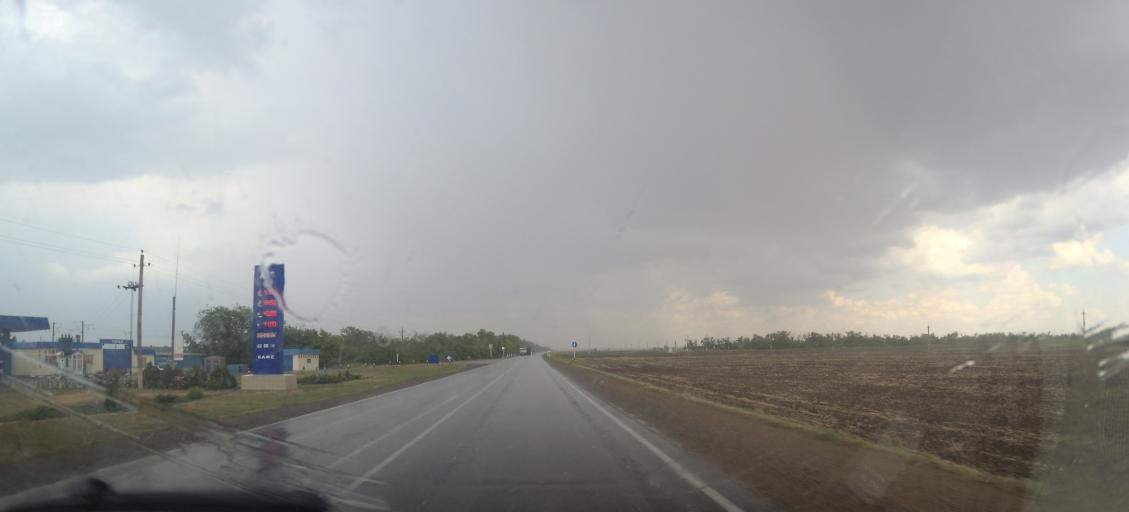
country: RU
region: Rostov
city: Proletarsk
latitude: 46.6481
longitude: 41.6756
